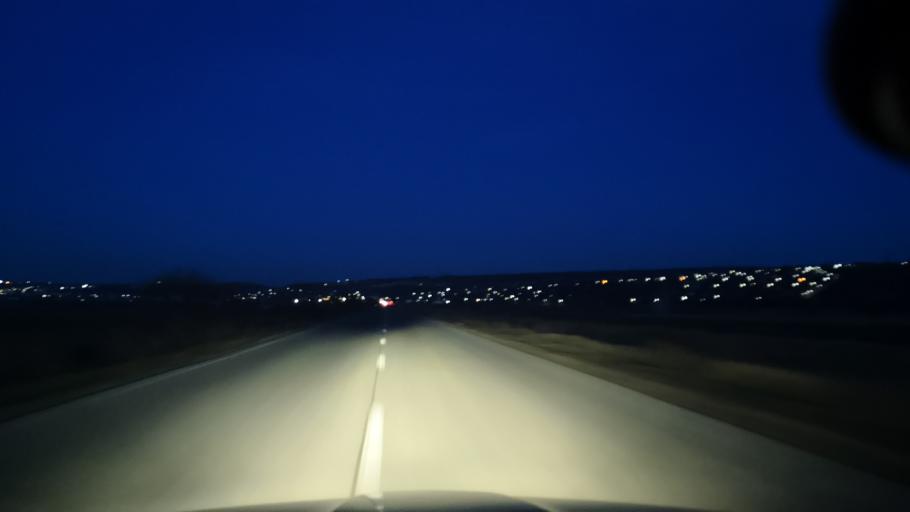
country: MD
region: Orhei
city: Orhei
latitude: 47.3471
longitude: 28.7907
